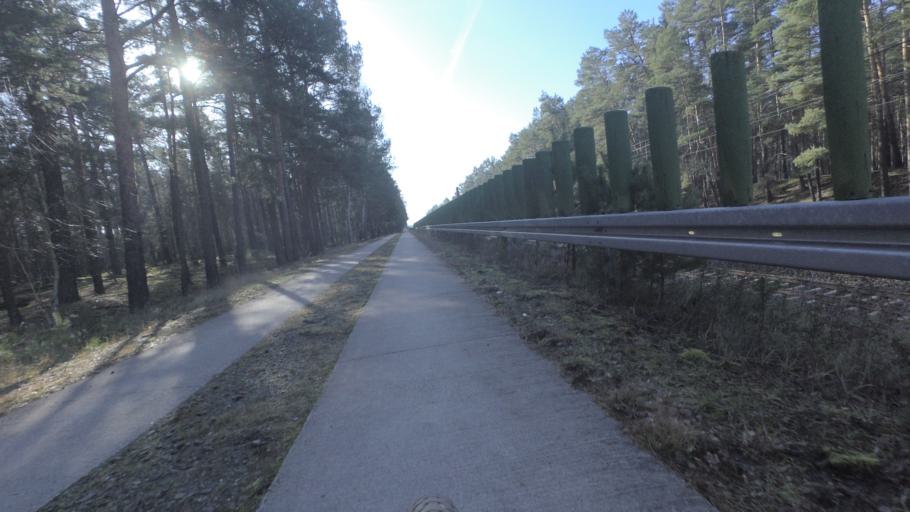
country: DE
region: Brandenburg
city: Trebbin
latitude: 52.1588
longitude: 13.2206
